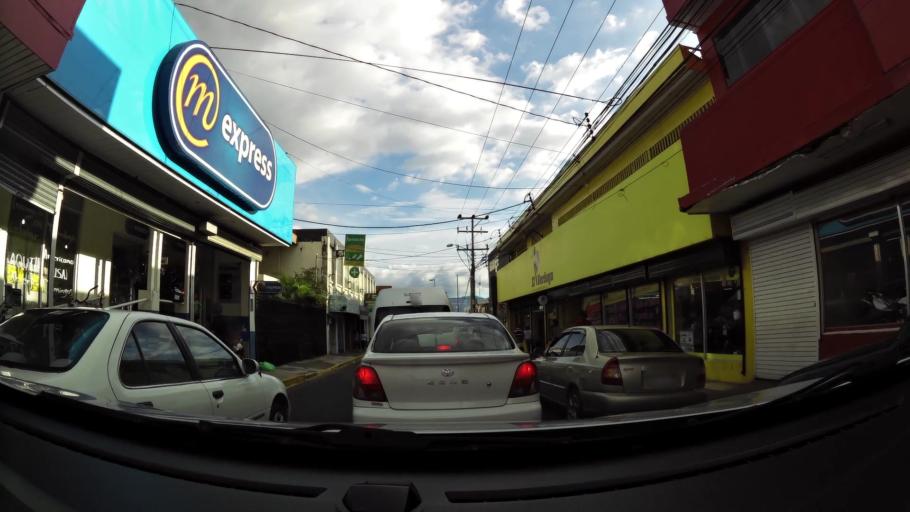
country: CR
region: Alajuela
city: Alajuela
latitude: 10.0171
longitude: -84.2154
